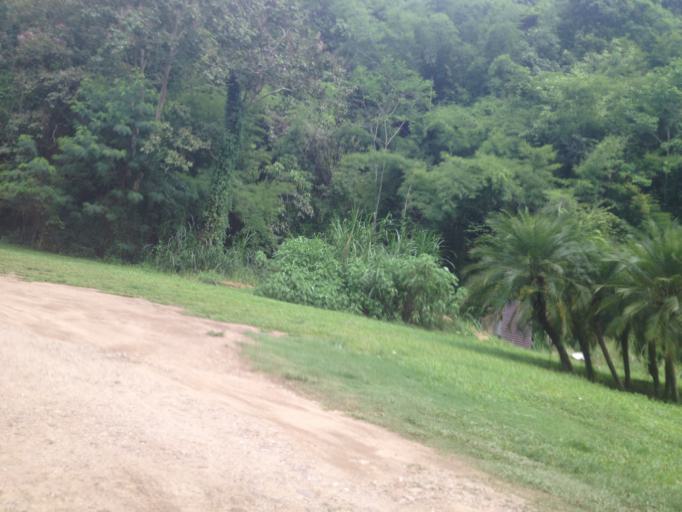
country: TH
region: Chiang Mai
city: Hang Dong
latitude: 18.7557
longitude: 98.8777
